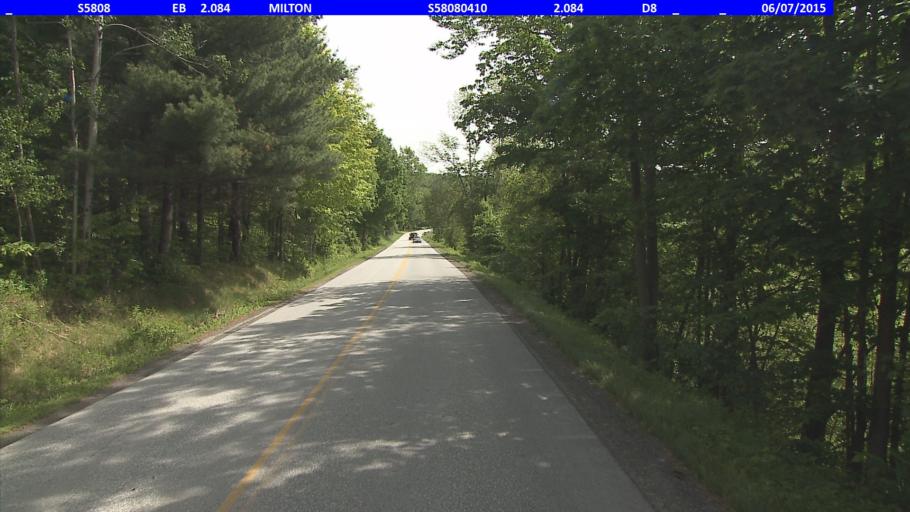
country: US
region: Vermont
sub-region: Chittenden County
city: Milton
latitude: 44.6419
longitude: -73.0763
